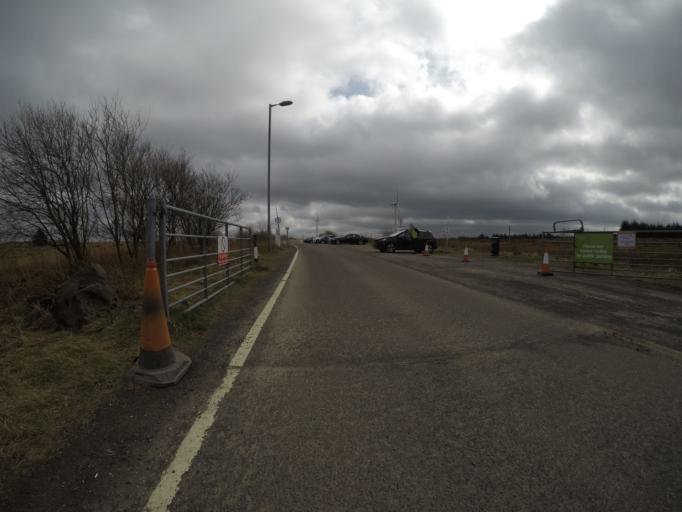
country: GB
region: Scotland
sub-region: East Renfrewshire
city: Newton Mearns
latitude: 55.7072
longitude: -4.3596
